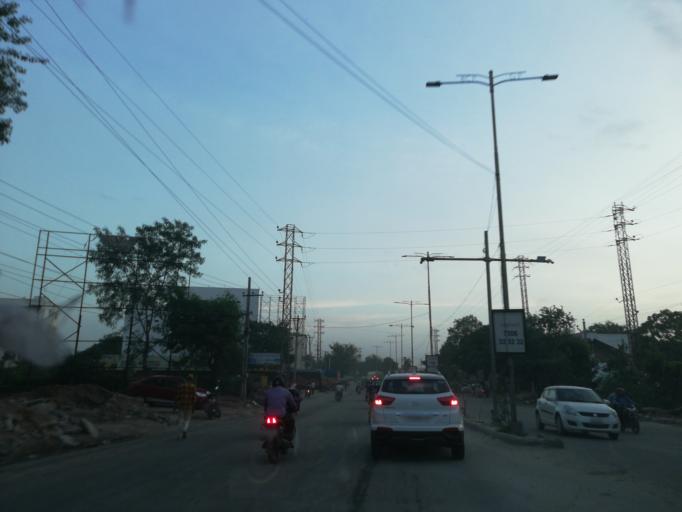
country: IN
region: Telangana
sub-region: Medak
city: Serilingampalle
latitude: 17.5344
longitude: 78.3576
